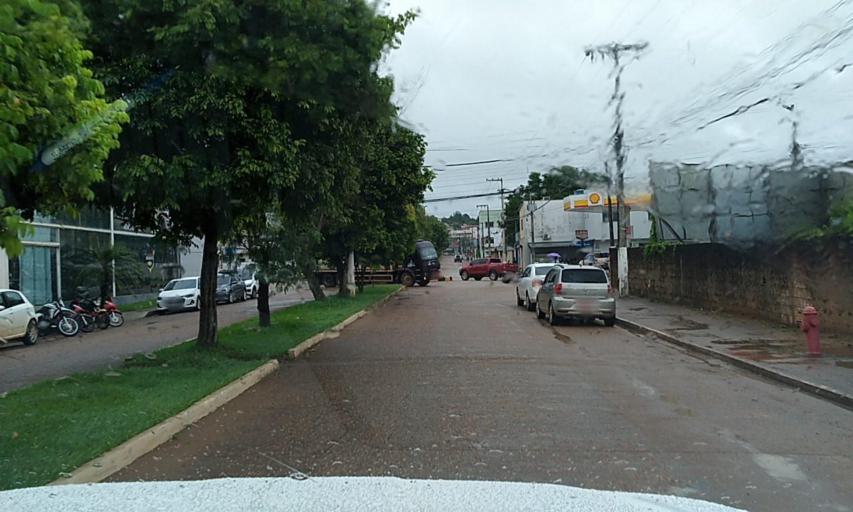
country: BR
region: Para
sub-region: Altamira
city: Altamira
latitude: -3.2116
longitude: -52.2240
